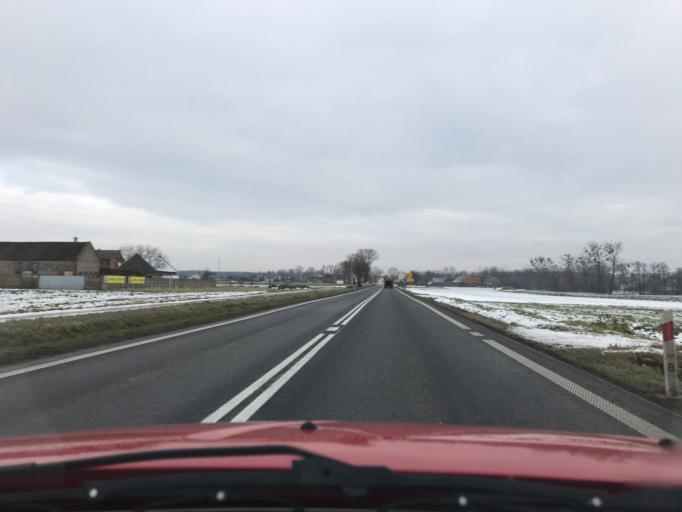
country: PL
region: Greater Poland Voivodeship
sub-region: Powiat pleszewski
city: Pleszew
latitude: 51.8877
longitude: 17.8505
